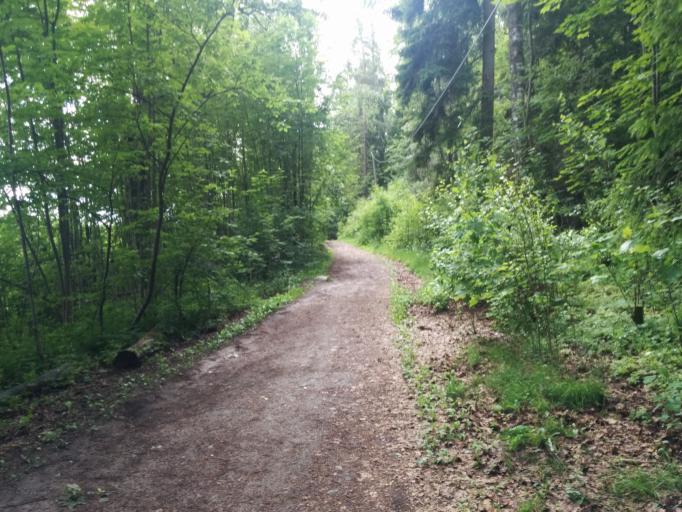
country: FI
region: Uusimaa
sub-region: Helsinki
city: Vantaa
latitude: 60.2412
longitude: 25.1271
